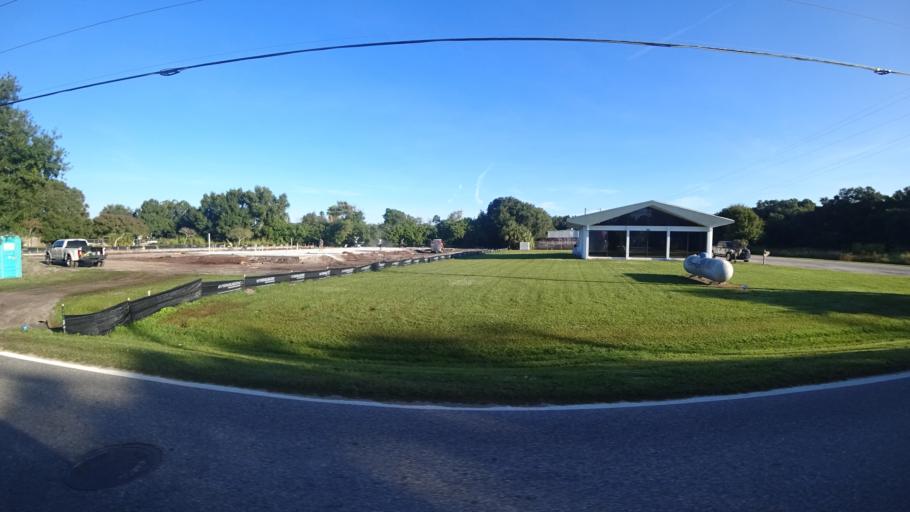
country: US
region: Florida
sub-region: Manatee County
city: Memphis
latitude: 27.5579
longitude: -82.5552
